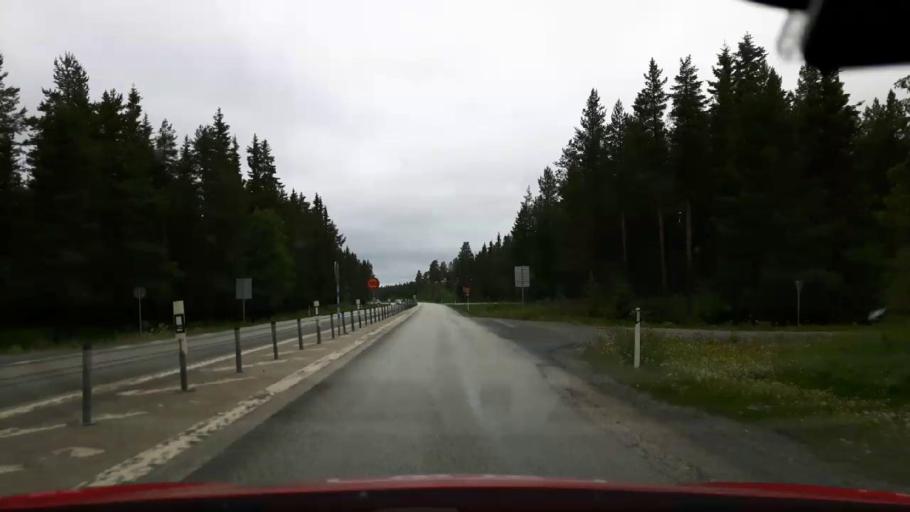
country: SE
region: Jaemtland
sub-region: OEstersunds Kommun
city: Brunflo
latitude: 63.1293
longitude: 14.7922
